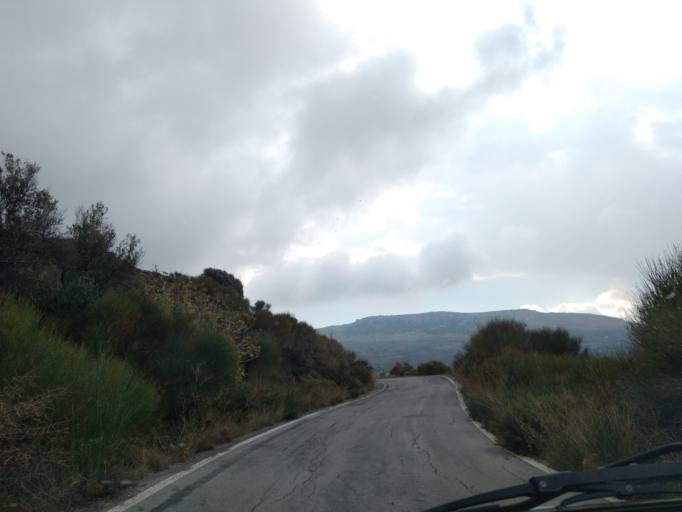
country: GR
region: Crete
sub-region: Nomos Lasithiou
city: Siteia
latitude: 35.1465
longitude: 26.0213
